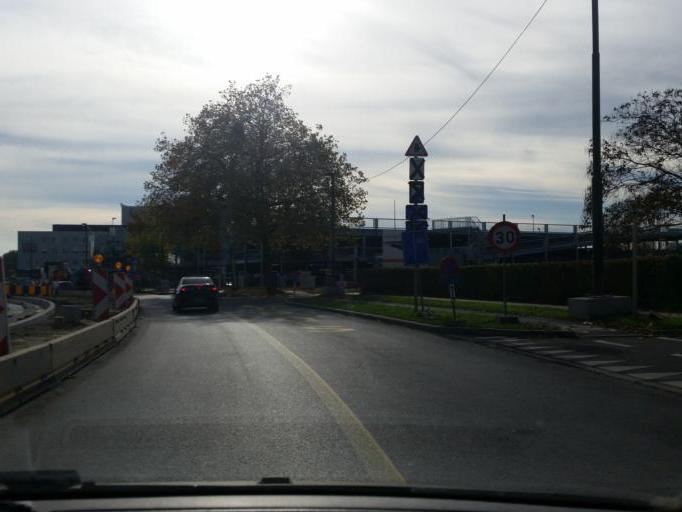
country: BE
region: Flanders
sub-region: Provincie Vlaams-Brabant
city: Wemmel
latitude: 50.8909
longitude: 4.3088
